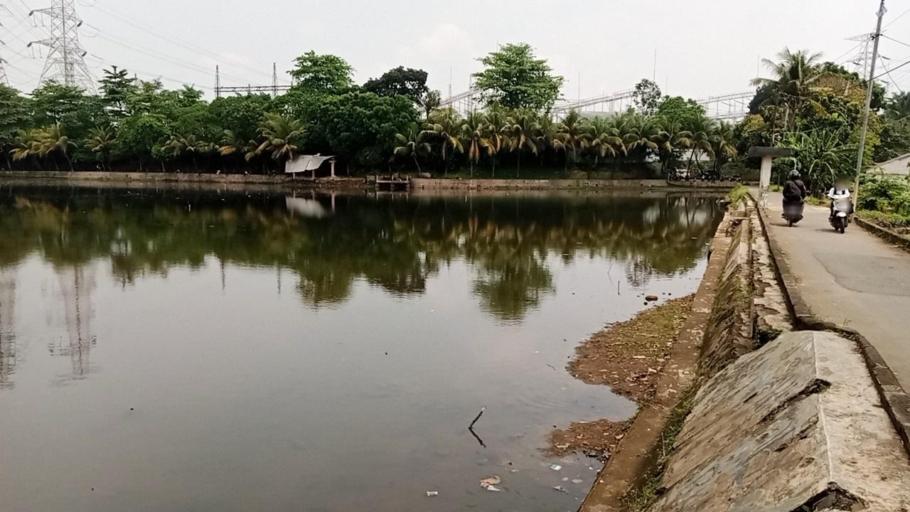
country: ID
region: West Java
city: Sawangan
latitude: -6.4120
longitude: 106.7959
